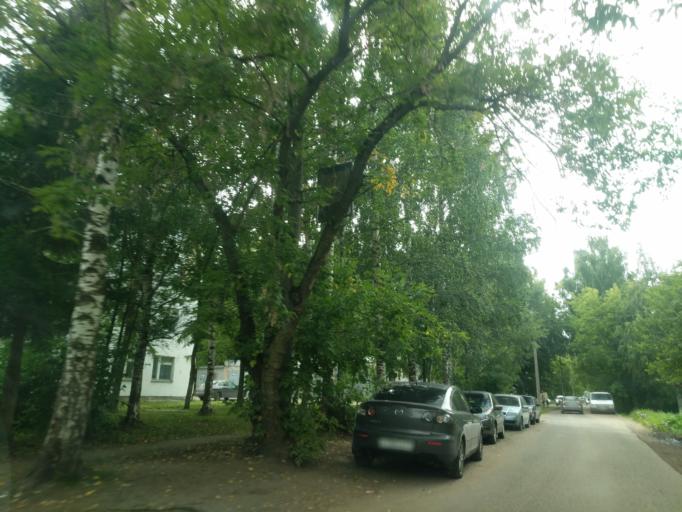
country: RU
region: Kirov
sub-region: Kirovo-Chepetskiy Rayon
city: Kirov
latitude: 58.5972
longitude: 49.6452
